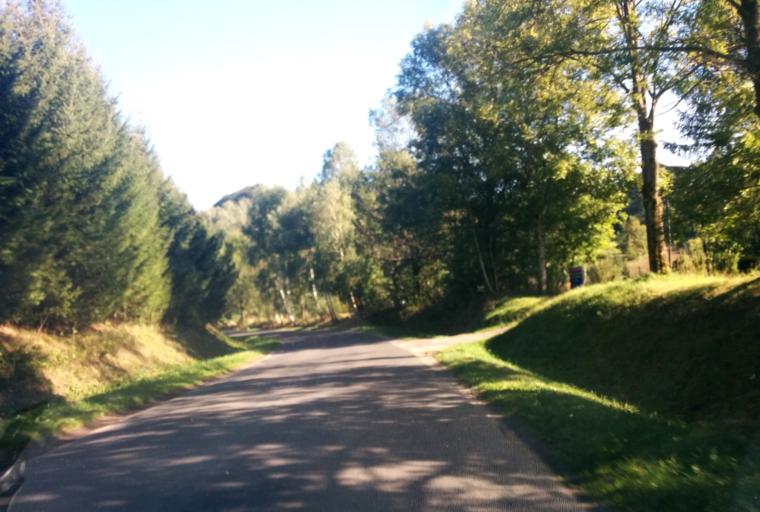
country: PL
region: Subcarpathian Voivodeship
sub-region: Powiat leski
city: Polanczyk
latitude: 49.3041
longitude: 22.4131
